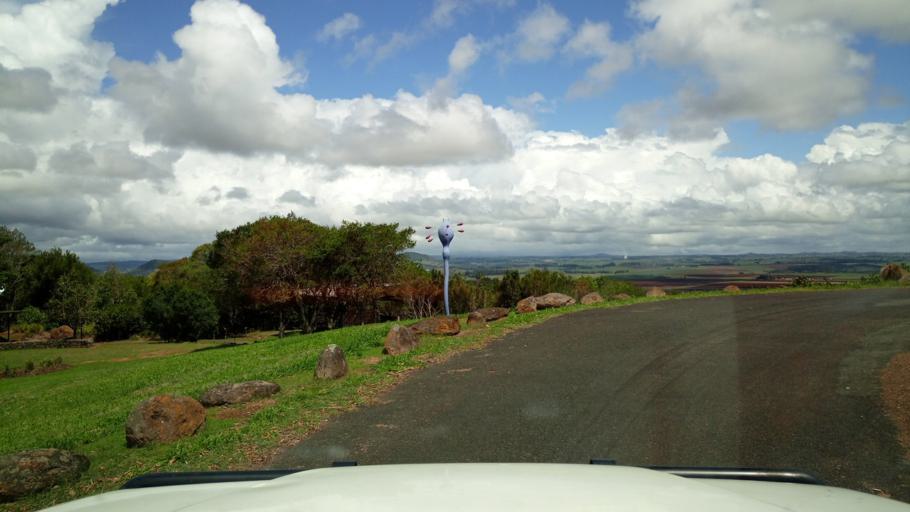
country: AU
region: Queensland
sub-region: Tablelands
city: Atherton
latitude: -17.2679
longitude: 145.4942
